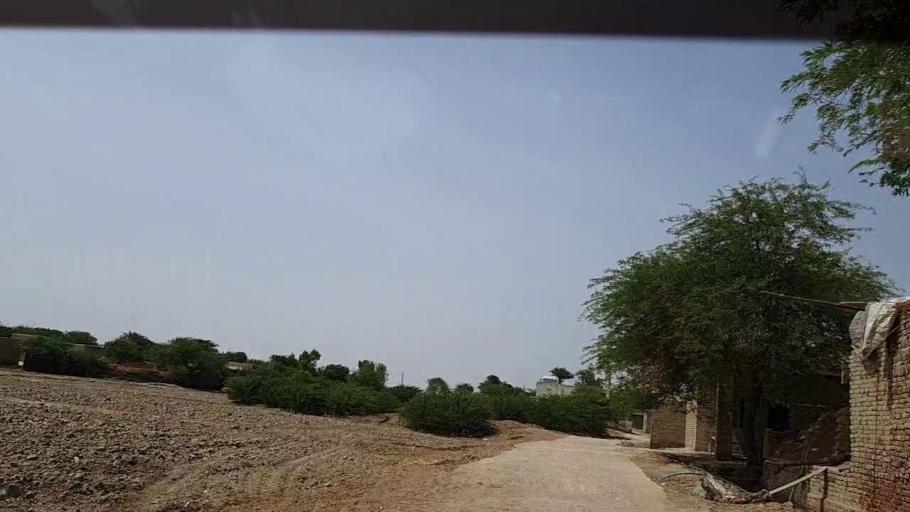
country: PK
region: Sindh
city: Johi
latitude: 26.7867
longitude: 67.6200
